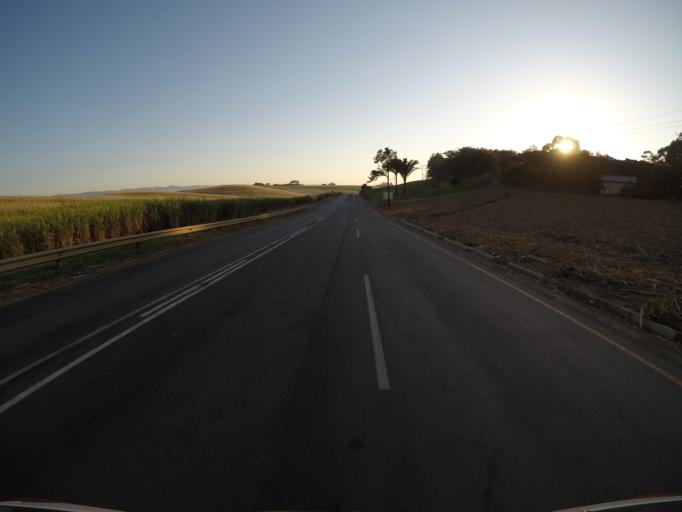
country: ZA
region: KwaZulu-Natal
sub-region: uThungulu District Municipality
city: eSikhawini
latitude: -28.9377
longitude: 31.7409
